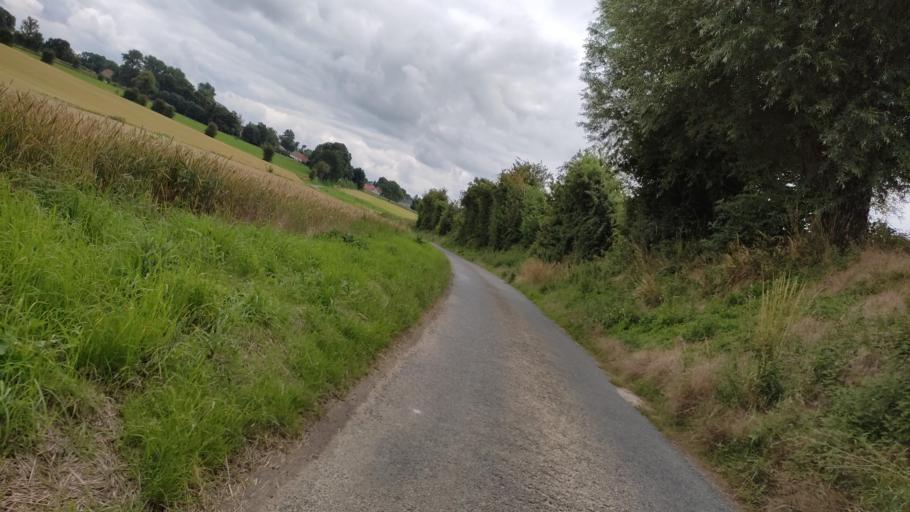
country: FR
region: Nord-Pas-de-Calais
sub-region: Departement du Pas-de-Calais
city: Beaumetz-les-Loges
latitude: 50.2464
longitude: 2.6338
